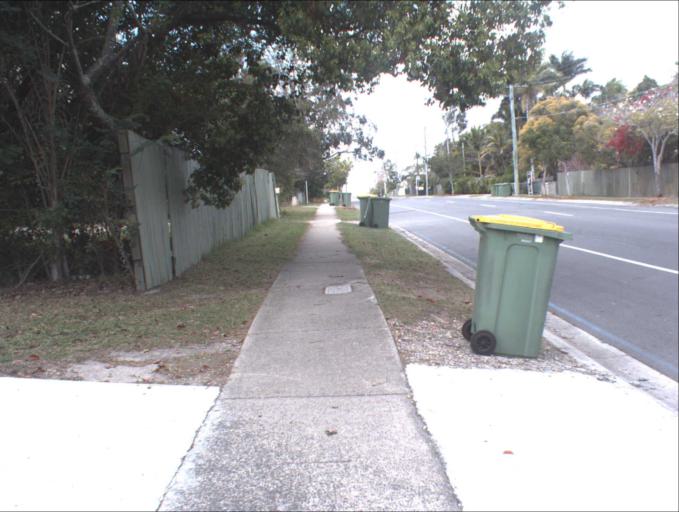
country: AU
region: Queensland
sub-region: Logan
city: Waterford West
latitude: -27.6745
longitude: 153.1239
